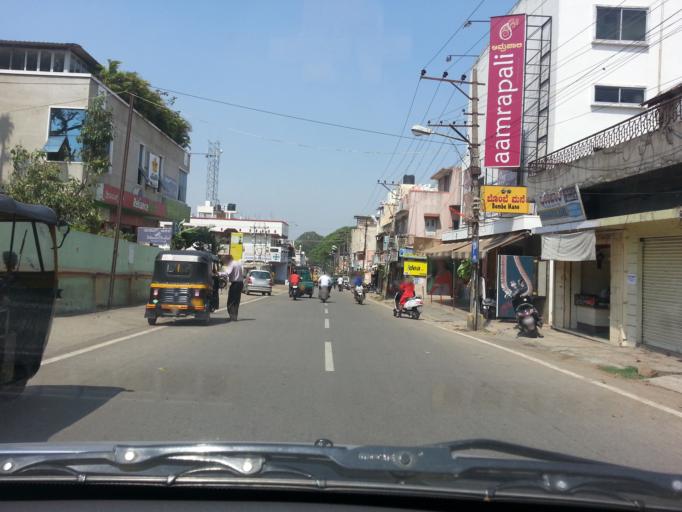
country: IN
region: Karnataka
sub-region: Mysore
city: Mysore
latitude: 12.3084
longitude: 76.6668
